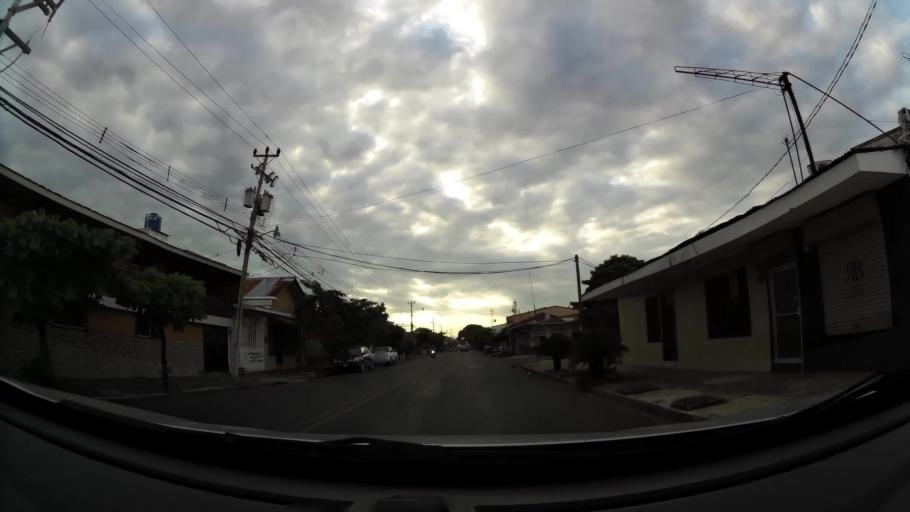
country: CR
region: Puntarenas
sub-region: Canton Central de Puntarenas
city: Puntarenas
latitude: 9.9781
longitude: -84.8264
